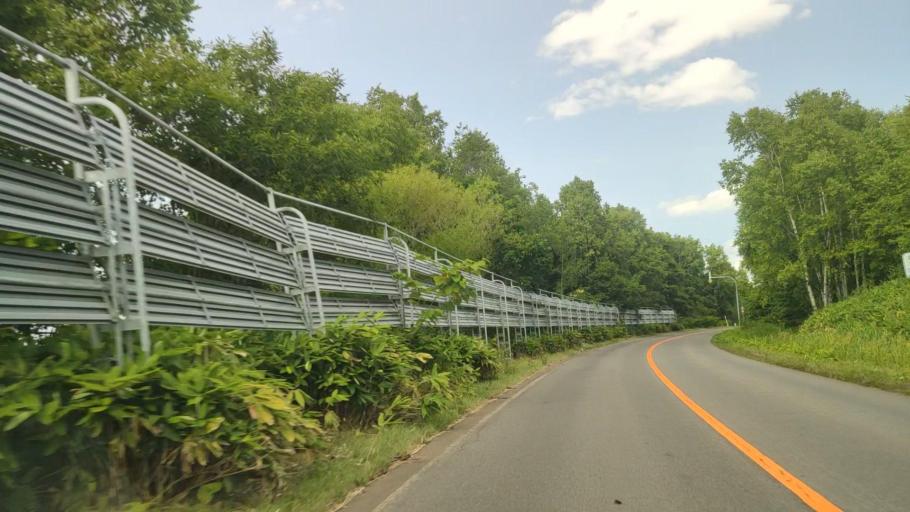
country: JP
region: Hokkaido
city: Nayoro
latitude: 44.2487
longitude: 142.4158
